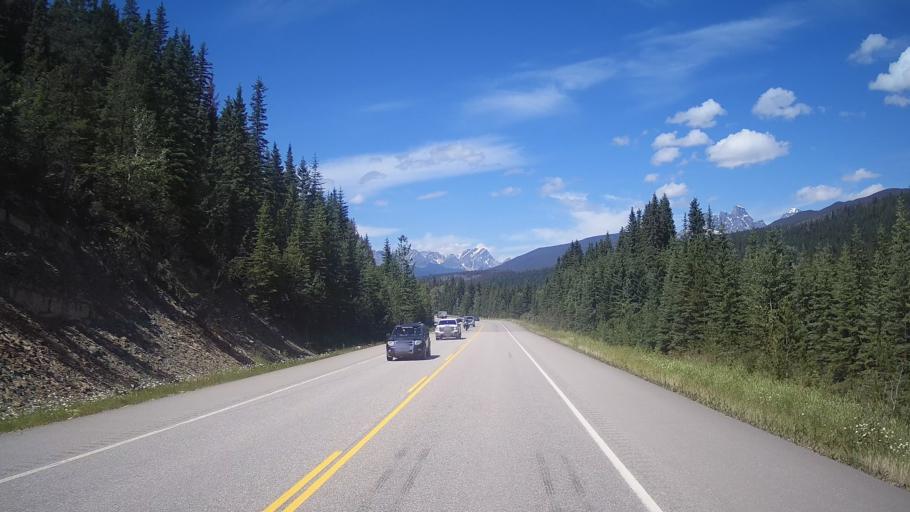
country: CA
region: Alberta
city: Jasper Park Lodge
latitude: 52.8813
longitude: -118.3556
